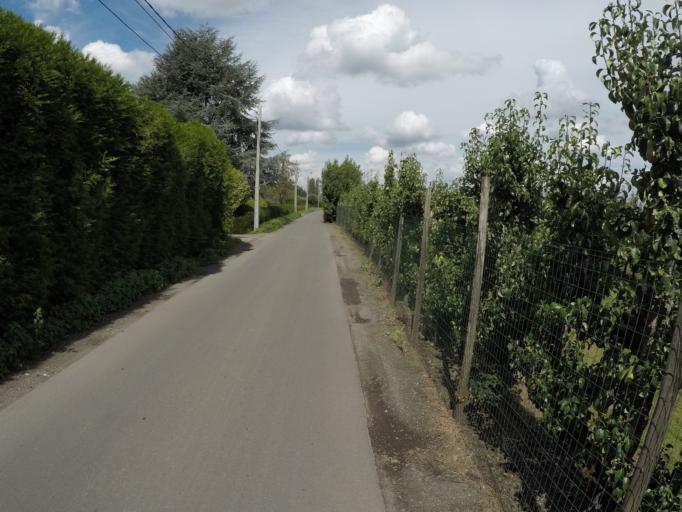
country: BE
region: Flanders
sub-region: Provincie Antwerpen
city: Ranst
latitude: 51.1749
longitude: 4.5454
